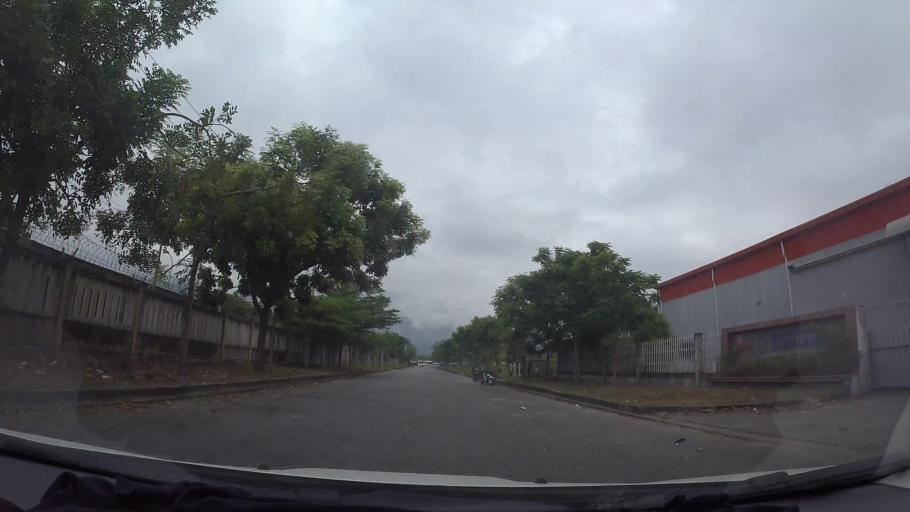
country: VN
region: Da Nang
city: Lien Chieu
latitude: 16.1260
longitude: 108.1173
